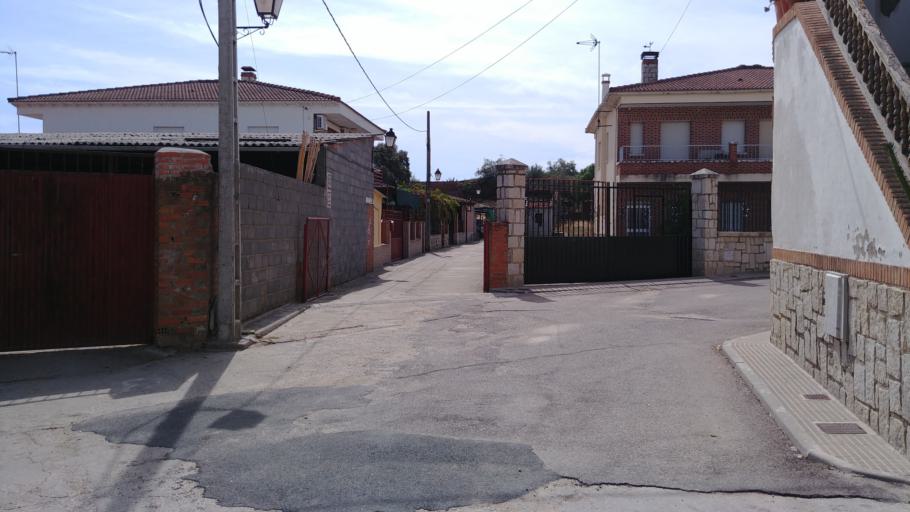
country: ES
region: Castille-La Mancha
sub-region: Province of Toledo
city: Navalcan
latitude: 40.0675
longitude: -5.0969
